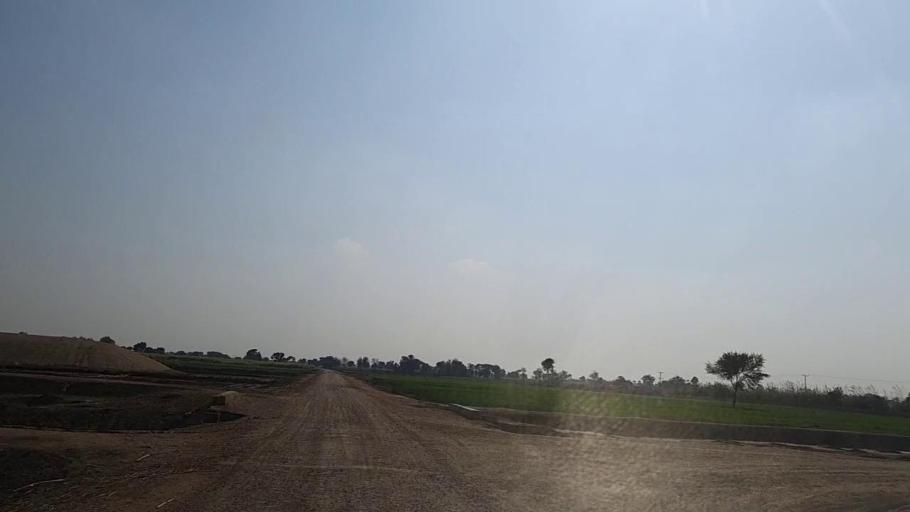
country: PK
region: Sindh
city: Daur
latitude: 26.4419
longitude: 68.2333
